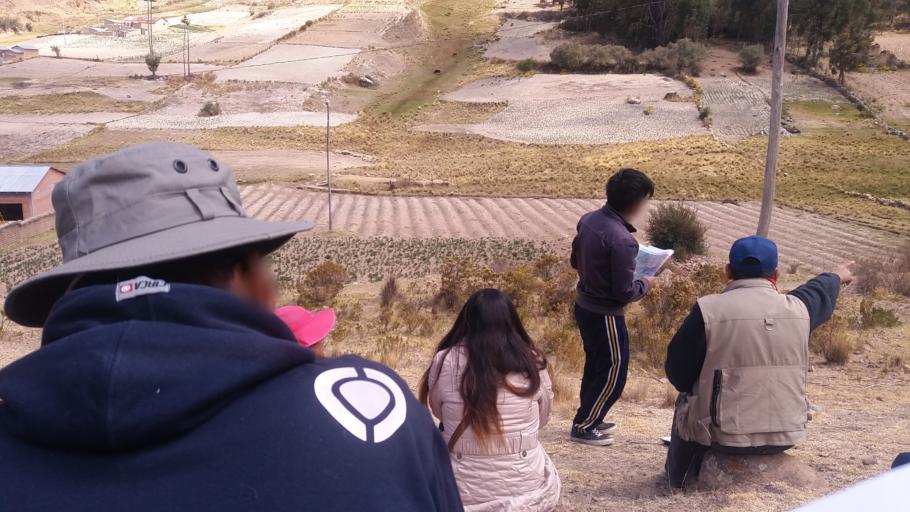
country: PE
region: Puno
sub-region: Yunguyo
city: Yunguyo
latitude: -16.1875
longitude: -69.0849
